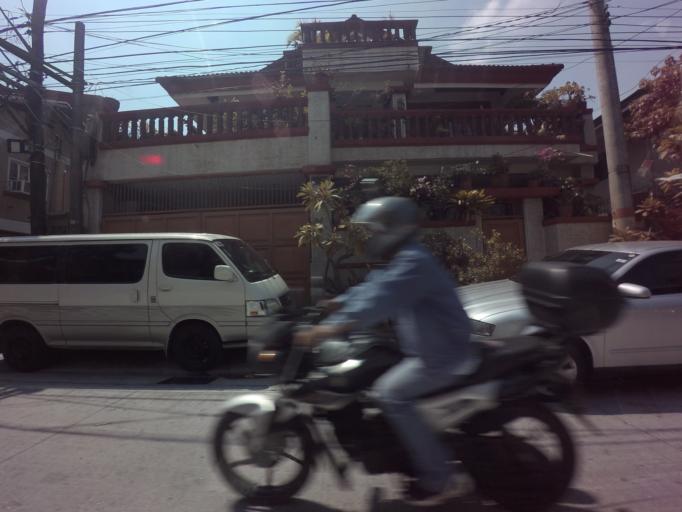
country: PH
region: Metro Manila
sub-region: Makati City
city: Makati City
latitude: 14.5647
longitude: 121.0059
